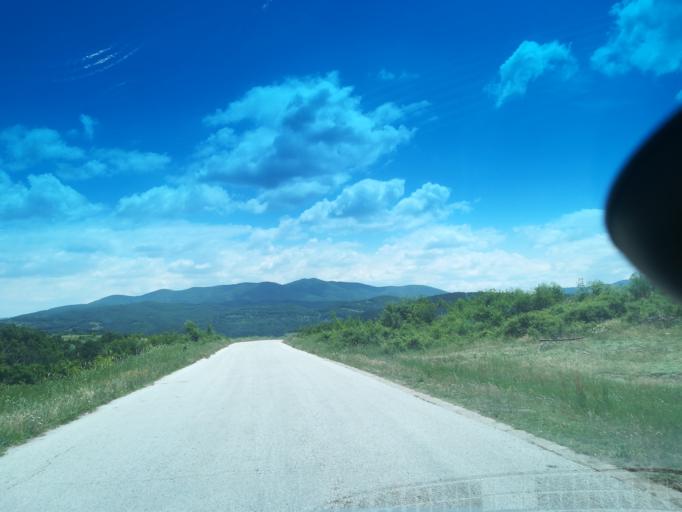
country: BG
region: Khaskovo
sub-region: Obshtina Mineralni Bani
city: Mineralni Bani
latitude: 41.9535
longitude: 25.2522
